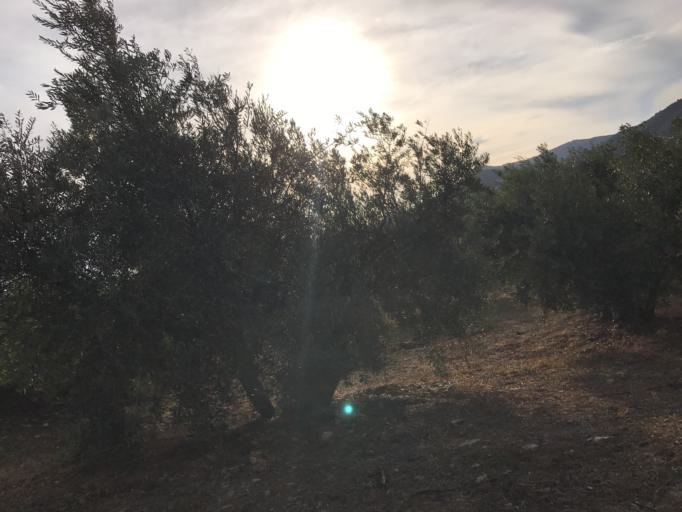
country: ES
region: Andalusia
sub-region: Provincia de Granada
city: Beas de Granada
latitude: 37.2203
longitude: -3.4727
